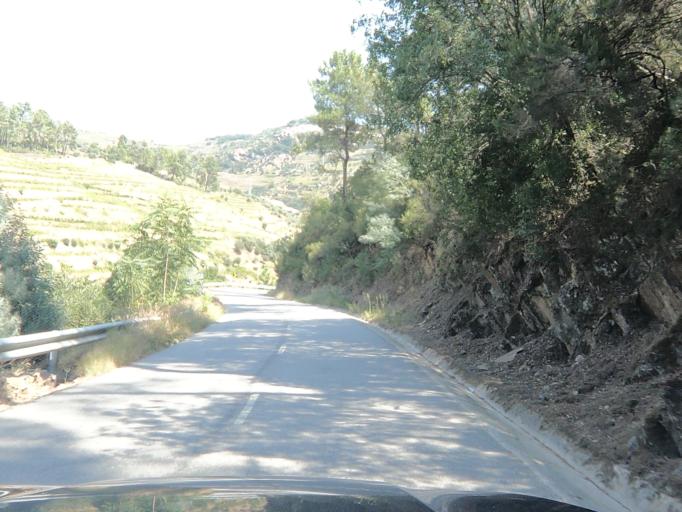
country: PT
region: Vila Real
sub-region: Sabrosa
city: Vilela
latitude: 41.1975
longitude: -7.5544
